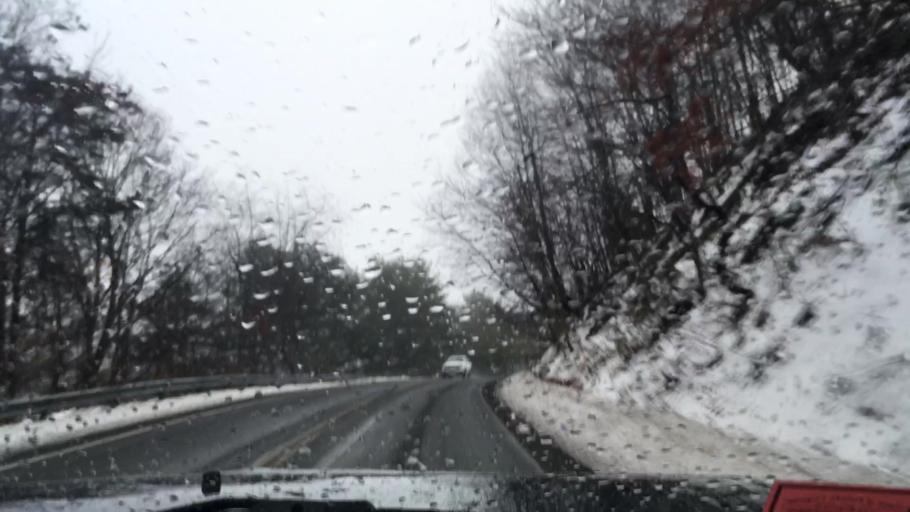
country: US
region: Virginia
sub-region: Pulaski County
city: Pulaski
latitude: 37.0278
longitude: -80.7178
